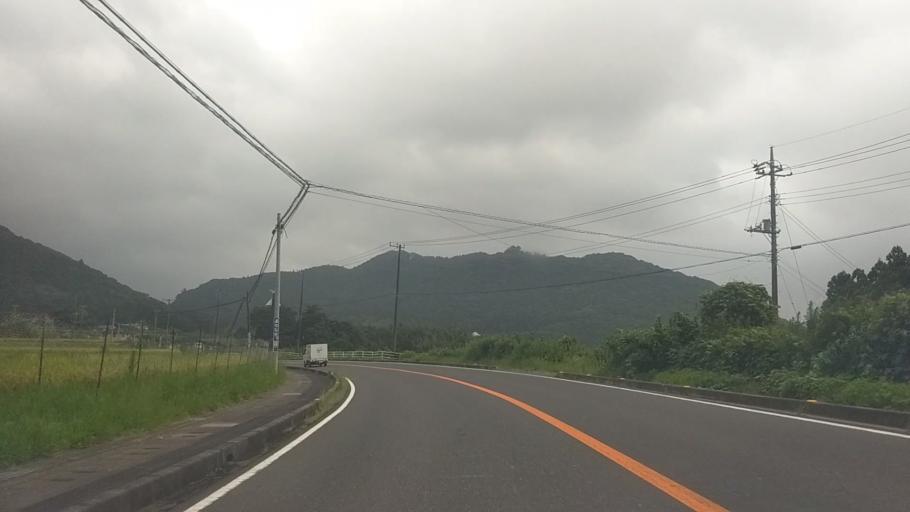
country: JP
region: Chiba
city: Kawaguchi
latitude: 35.1348
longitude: 140.0727
